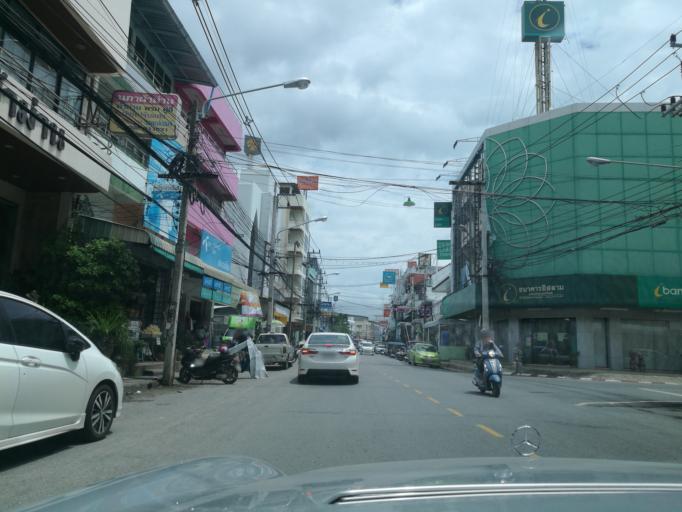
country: TH
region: Prachuap Khiri Khan
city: Prachuap Khiri Khan
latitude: 11.8019
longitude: 99.7981
